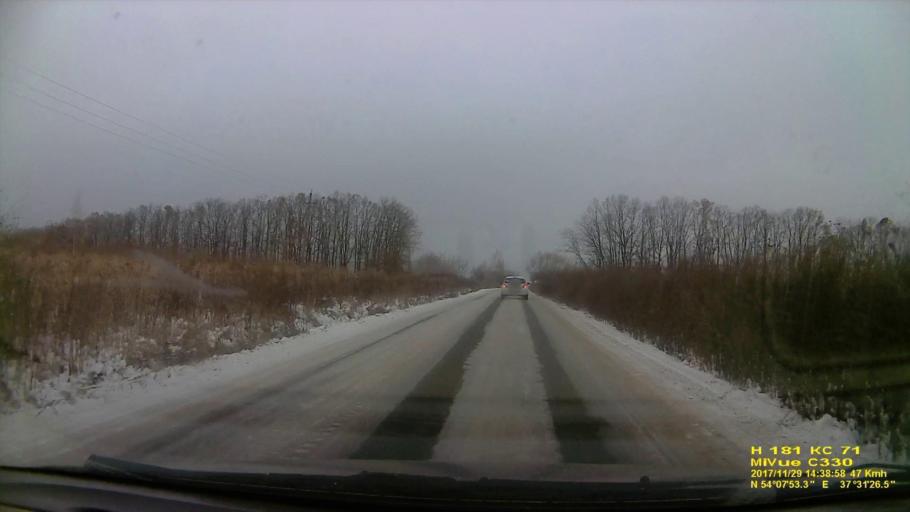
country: RU
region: Tula
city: Kosaya Gora
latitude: 54.1313
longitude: 37.5239
